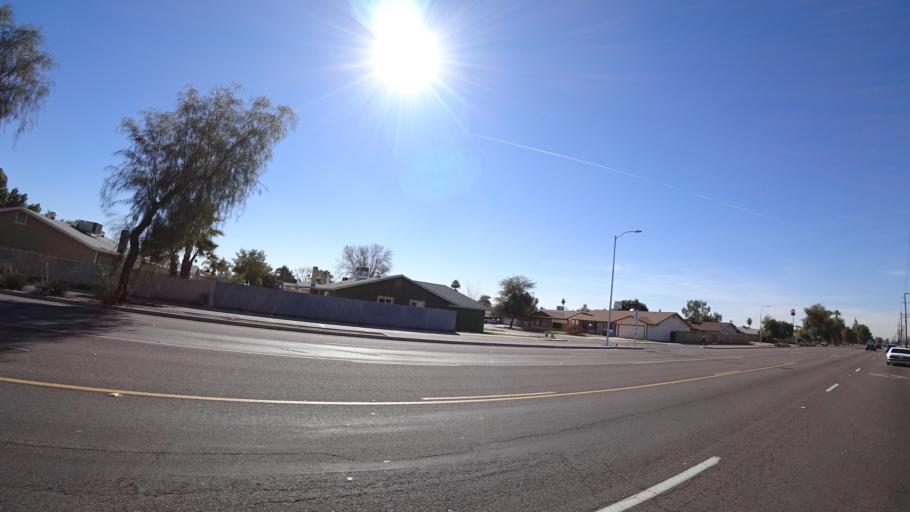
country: US
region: Arizona
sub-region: Maricopa County
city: Glendale
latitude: 33.5095
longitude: -112.1963
